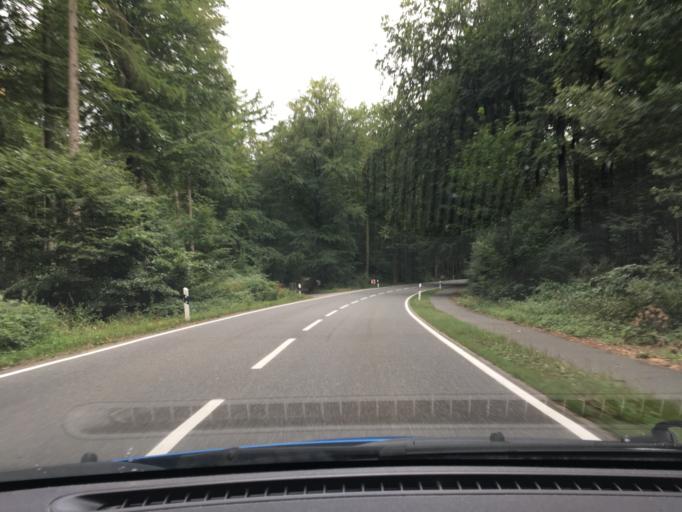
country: DE
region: Lower Saxony
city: Bendestorf
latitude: 53.3411
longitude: 9.9430
